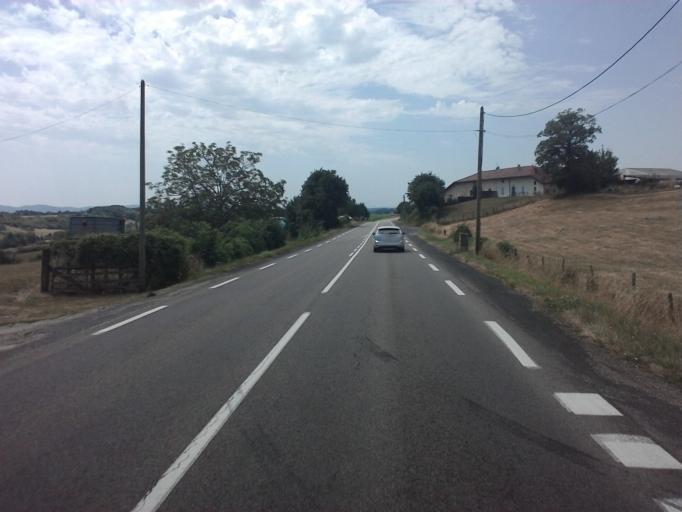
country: FR
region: Rhone-Alpes
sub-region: Departement de l'Ain
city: Coligny
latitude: 46.3716
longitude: 5.3397
